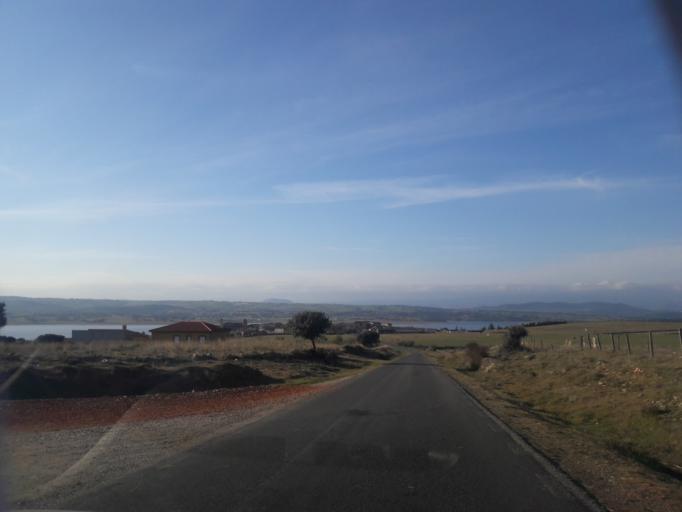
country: ES
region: Castille and Leon
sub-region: Provincia de Salamanca
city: Salvatierra de Tormes
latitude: 40.5967
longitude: -5.5993
